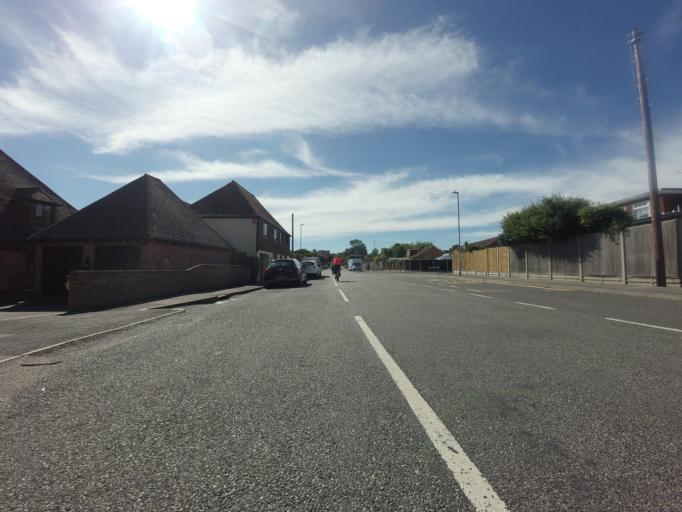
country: GB
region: England
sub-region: Kent
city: Birchington-on-Sea
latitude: 51.3403
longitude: 1.2760
